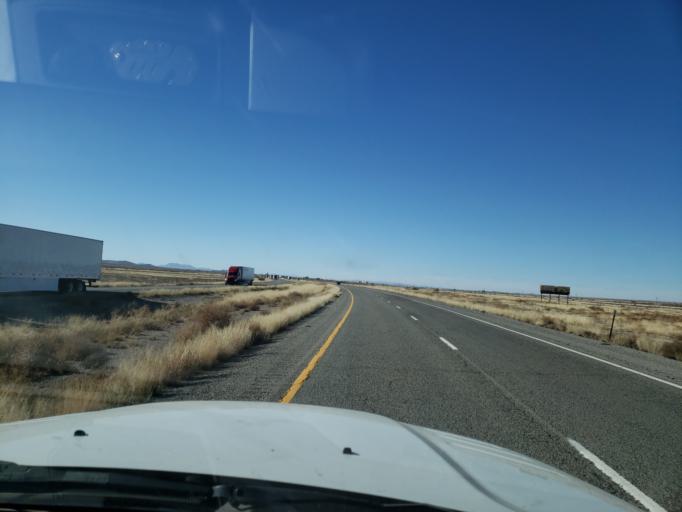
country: US
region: New Mexico
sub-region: Hidalgo County
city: Lordsburg
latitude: 32.3284
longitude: -108.6345
